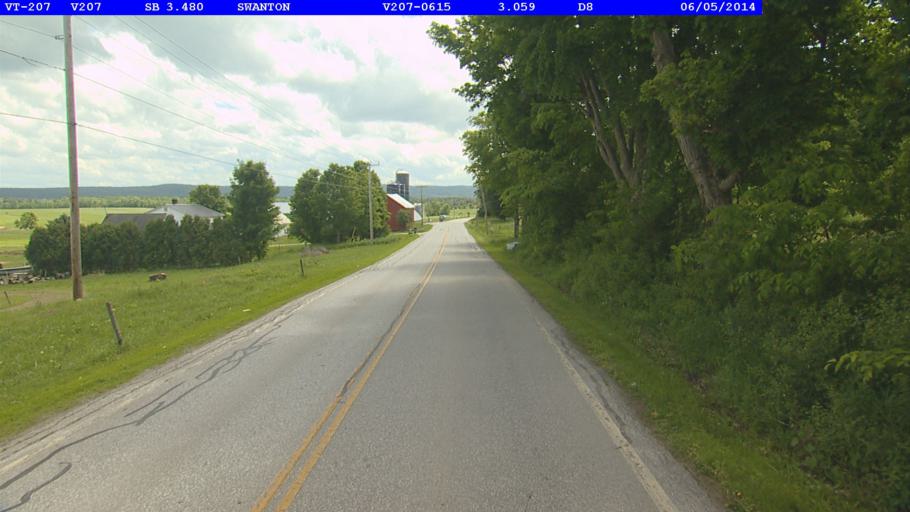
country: US
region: Vermont
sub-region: Franklin County
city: Swanton
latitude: 44.8882
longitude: -73.0678
